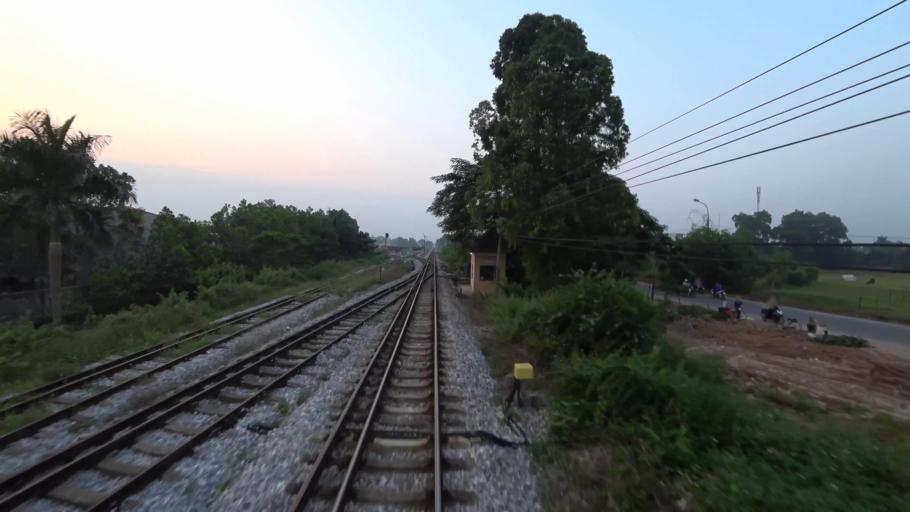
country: VN
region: Ha Noi
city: Dong Anh
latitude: 21.1382
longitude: 105.8682
